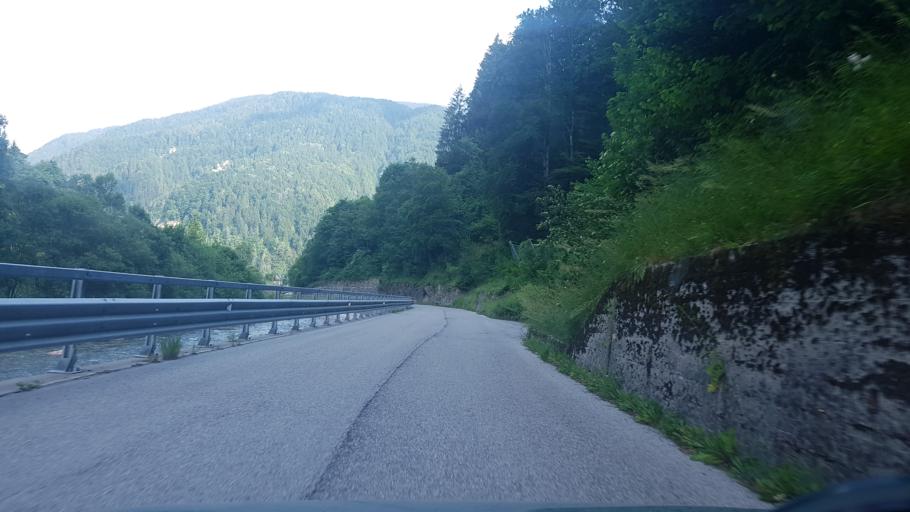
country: IT
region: Friuli Venezia Giulia
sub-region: Provincia di Udine
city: Pontebba
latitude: 46.5119
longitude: 13.2968
